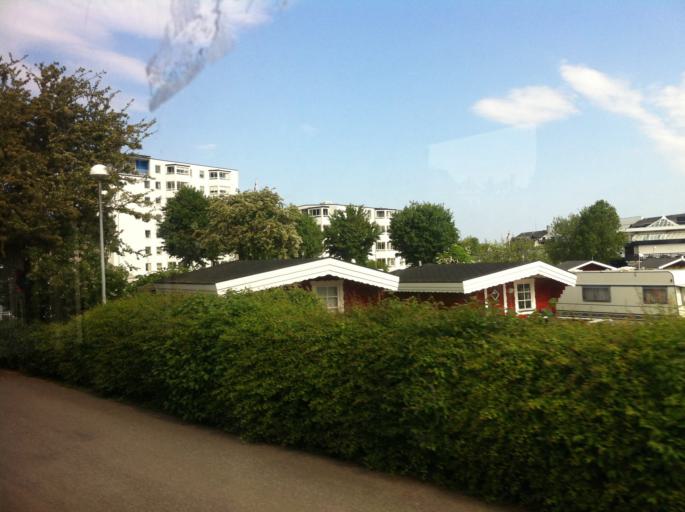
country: DK
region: Capital Region
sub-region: Helsingor Kommune
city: Helsingor
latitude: 56.0432
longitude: 12.6046
